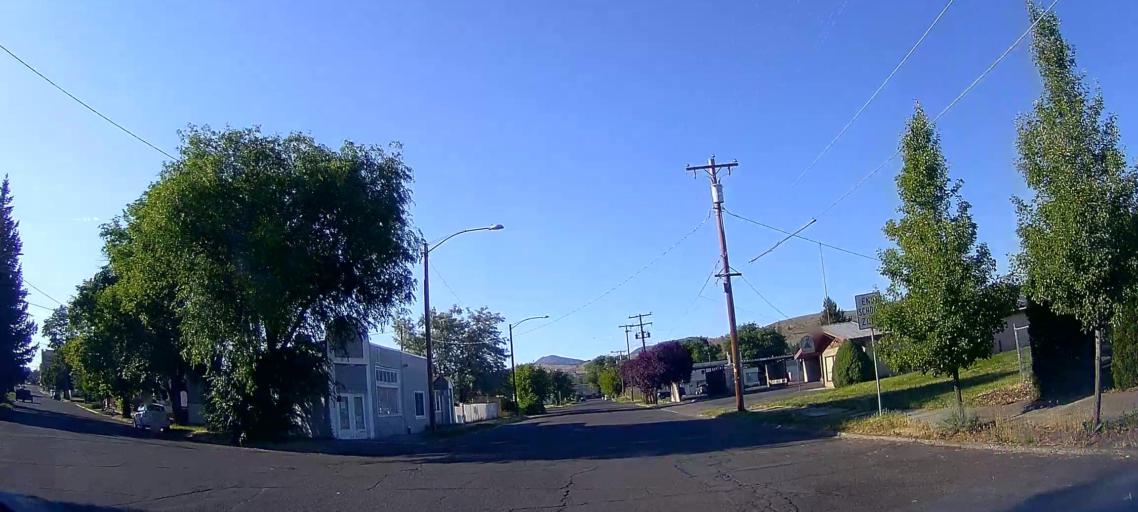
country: US
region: Oregon
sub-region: Klamath County
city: Klamath Falls
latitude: 42.2247
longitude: -121.7767
